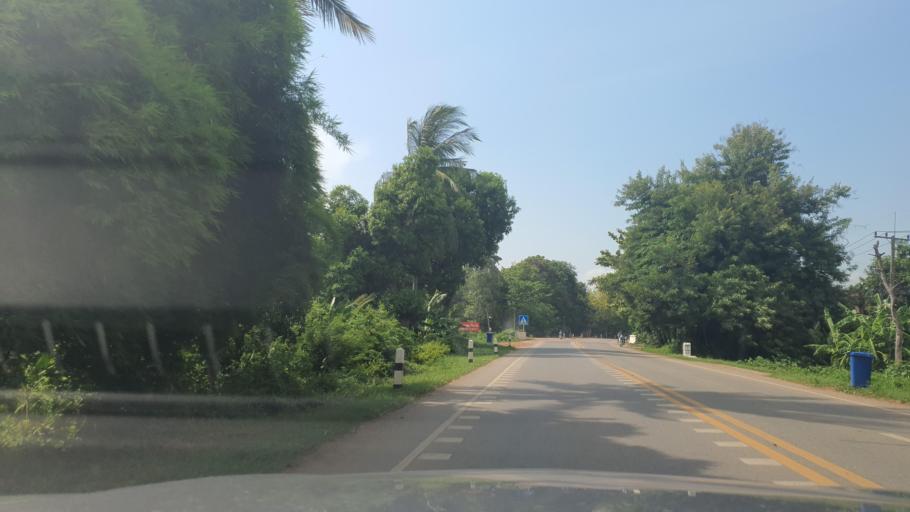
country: TH
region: Sukhothai
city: Si Samrong
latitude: 17.1453
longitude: 99.8239
